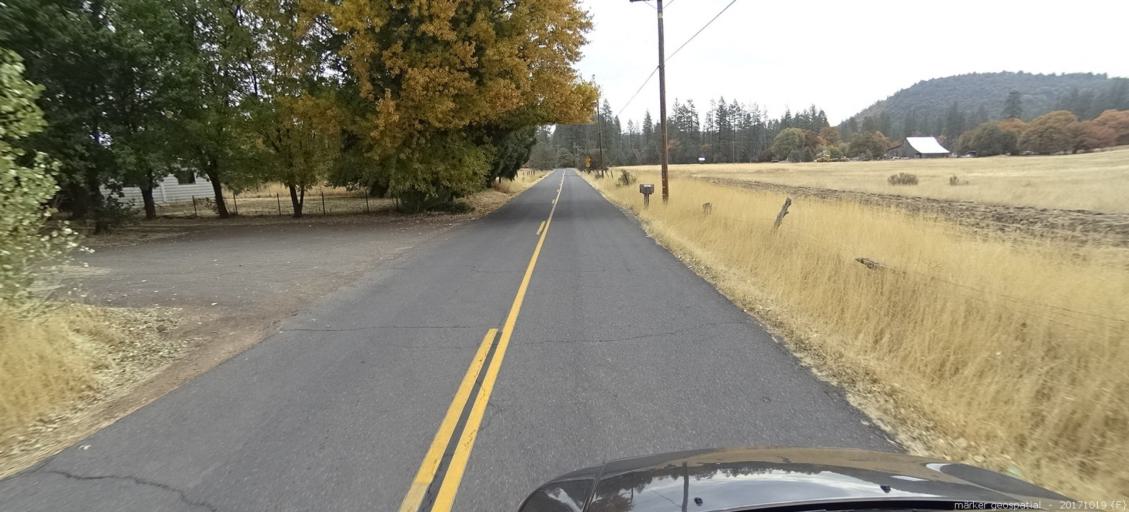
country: US
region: California
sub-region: Shasta County
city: Burney
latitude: 41.0660
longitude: -121.3345
